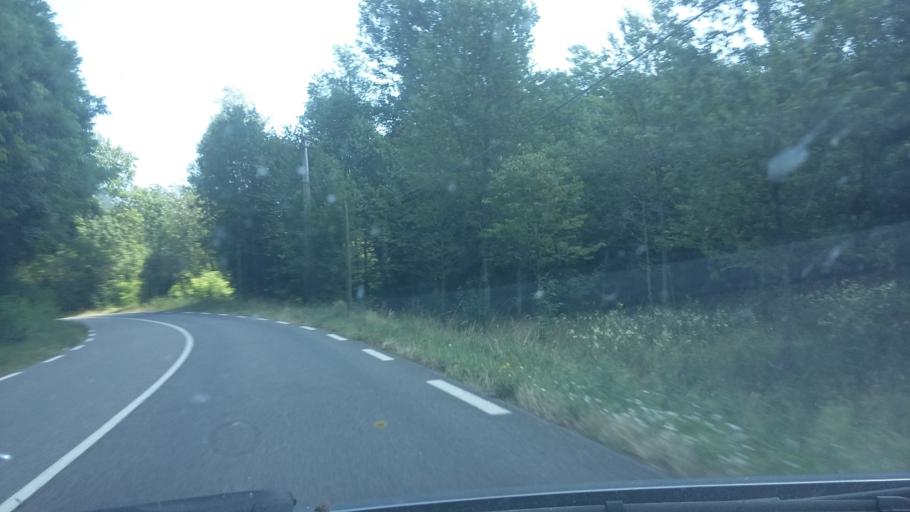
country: FR
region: Rhone-Alpes
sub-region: Departement de l'Ain
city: Virieu-le-Grand
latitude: 45.8204
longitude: 5.6437
